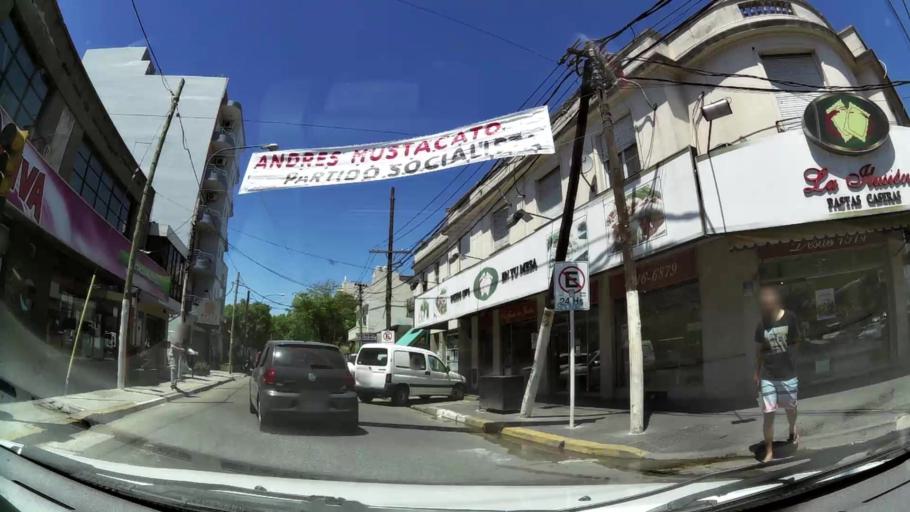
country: AR
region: Buenos Aires
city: Caseros
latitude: -34.6023
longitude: -58.5618
